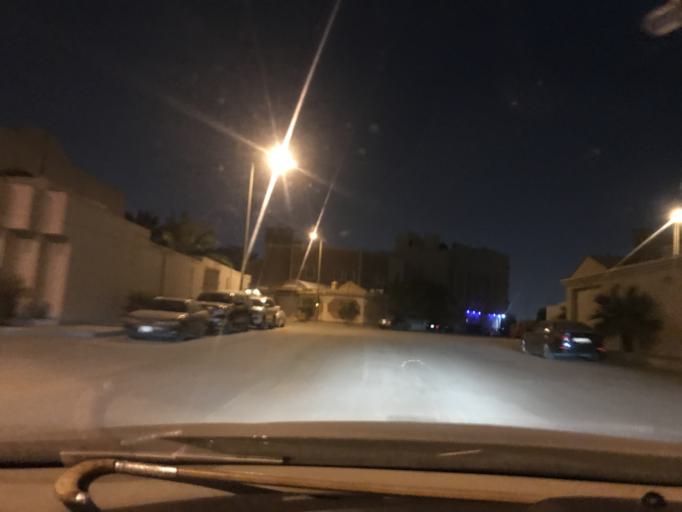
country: SA
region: Ar Riyad
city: Riyadh
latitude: 24.7555
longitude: 46.7538
